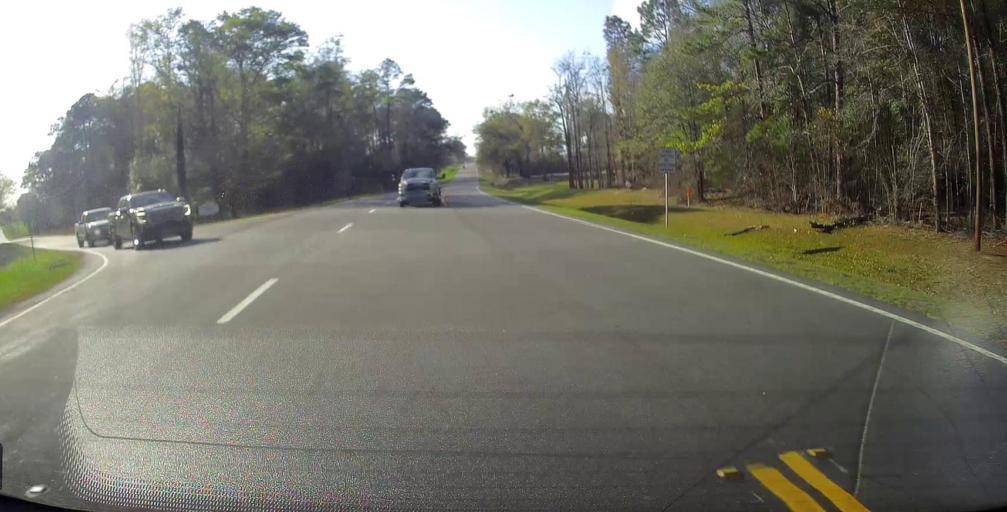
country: US
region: Georgia
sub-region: Montgomery County
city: Mount Vernon
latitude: 32.1803
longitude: -82.5562
